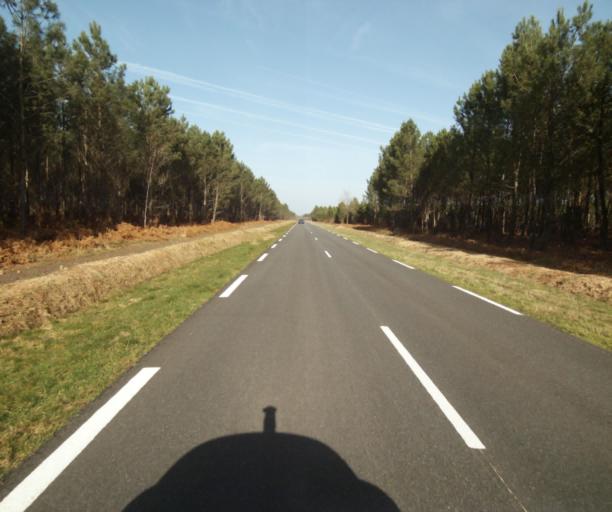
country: FR
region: Aquitaine
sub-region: Departement de la Gironde
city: Grignols
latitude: 44.1846
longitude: -0.0915
